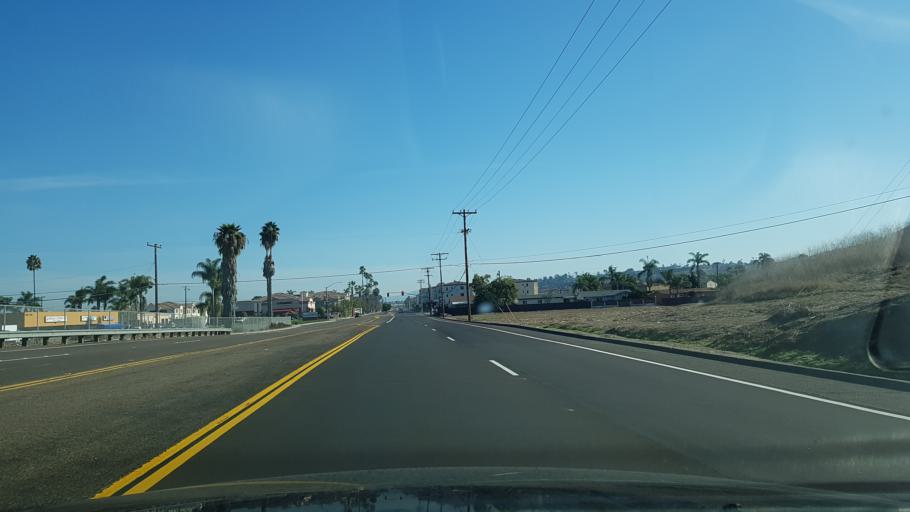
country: US
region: California
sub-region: San Diego County
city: Camp Pendleton South
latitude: 33.2121
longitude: -117.3501
